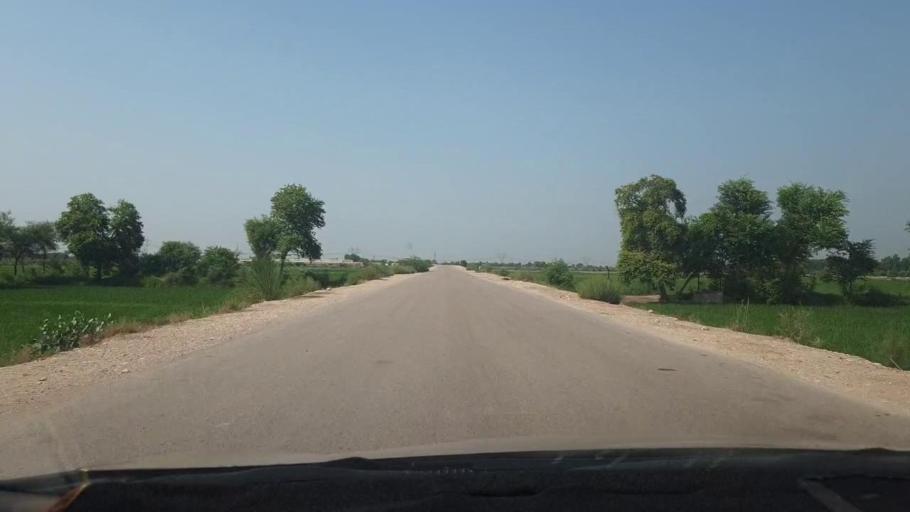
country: PK
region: Sindh
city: Larkana
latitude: 27.6008
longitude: 68.2431
